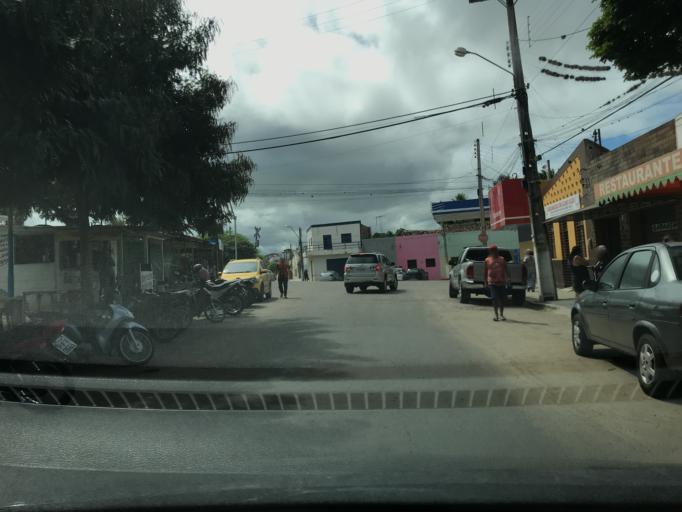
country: BR
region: Pernambuco
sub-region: Bezerros
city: Bezerros
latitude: -8.2333
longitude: -35.7537
